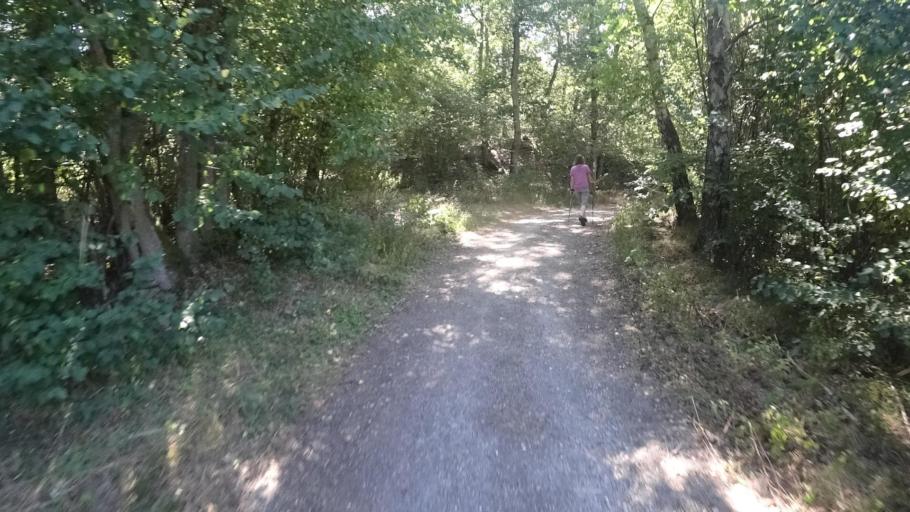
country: DE
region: Rheinland-Pfalz
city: Ohlweiler
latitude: 49.9563
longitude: 7.4955
